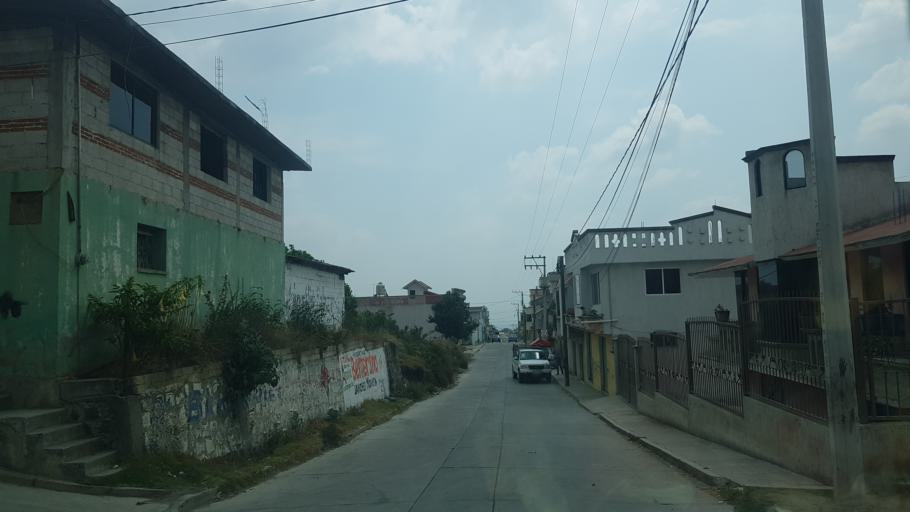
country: MX
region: Puebla
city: Domingo Arenas
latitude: 19.1358
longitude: -98.4920
